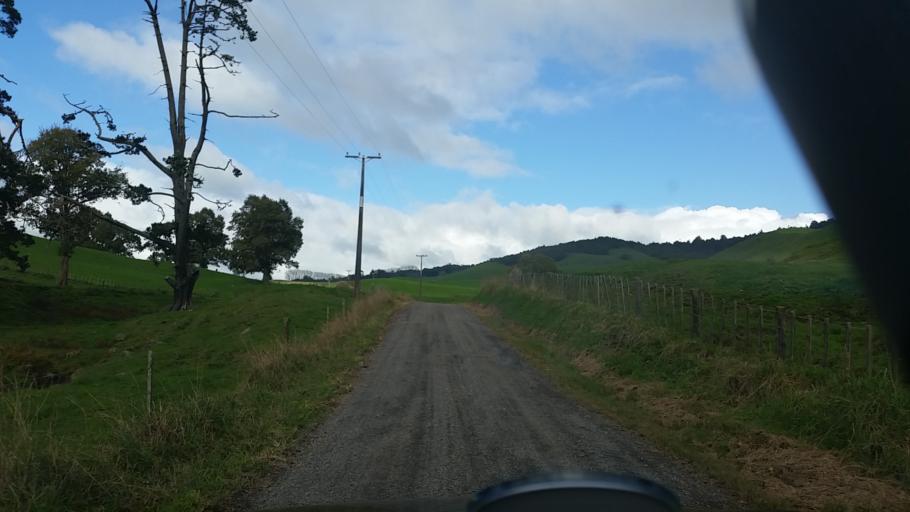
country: NZ
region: Waikato
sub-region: Matamata-Piako District
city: Matamata
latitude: -37.8147
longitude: 175.6732
